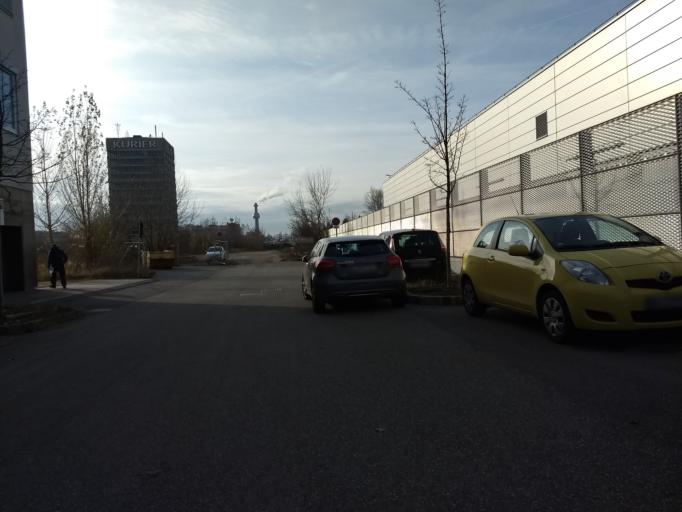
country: AT
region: Vienna
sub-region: Wien Stadt
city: Vienna
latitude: 48.2471
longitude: 16.3656
